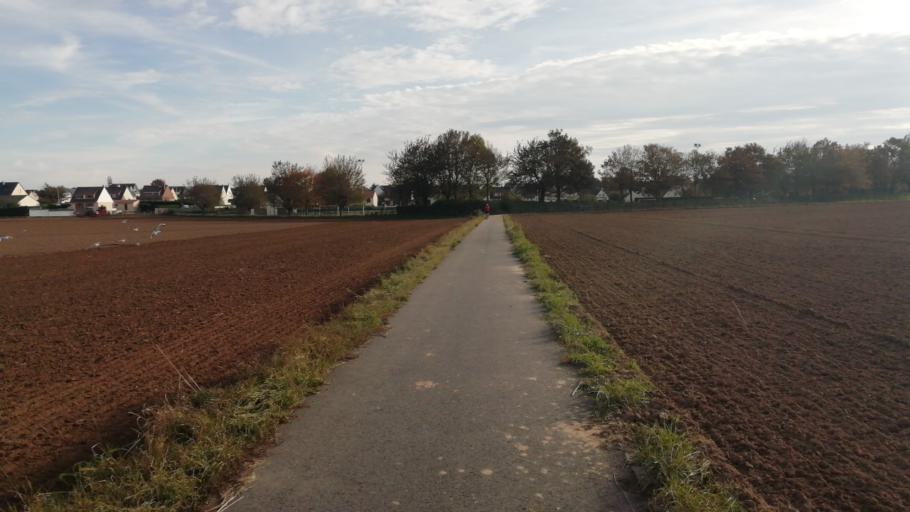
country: FR
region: Haute-Normandie
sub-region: Departement de la Seine-Maritime
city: Rogerville
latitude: 49.5087
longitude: 0.2640
